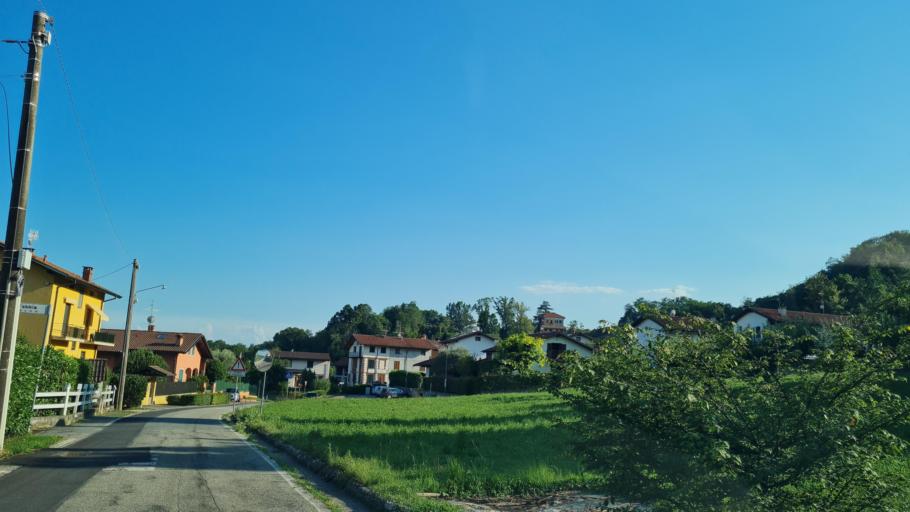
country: IT
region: Piedmont
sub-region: Provincia di Biella
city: Camburzano
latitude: 45.5504
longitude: 8.0073
